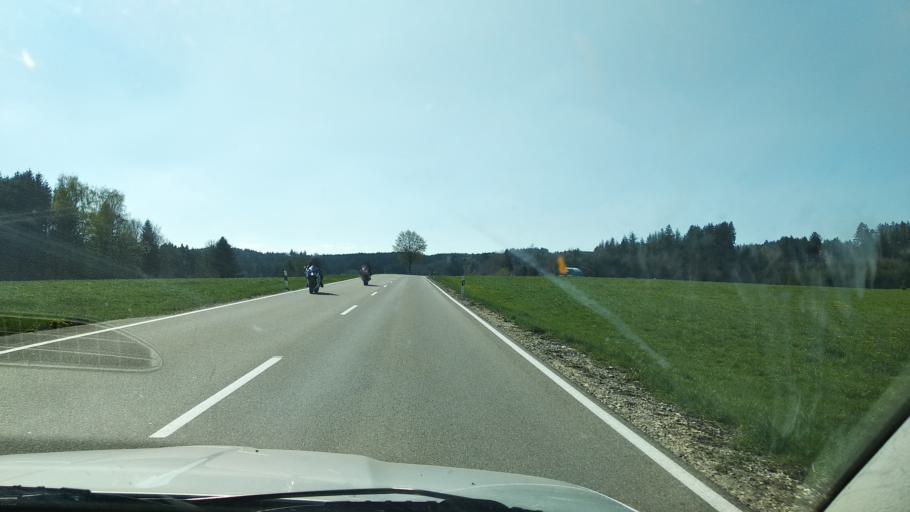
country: DE
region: Bavaria
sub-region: Swabia
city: Stetten
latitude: 48.0446
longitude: 10.4076
